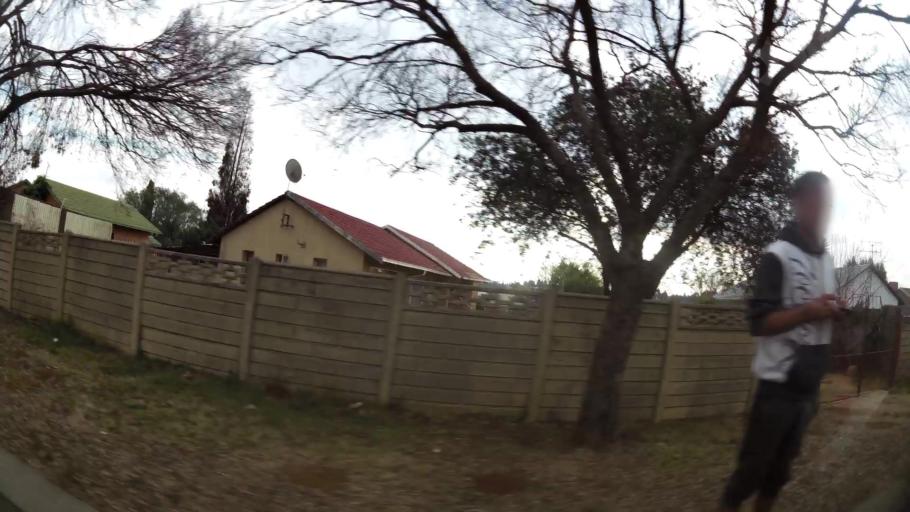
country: ZA
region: Gauteng
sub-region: Ekurhuleni Metropolitan Municipality
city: Benoni
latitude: -26.1294
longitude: 28.3607
